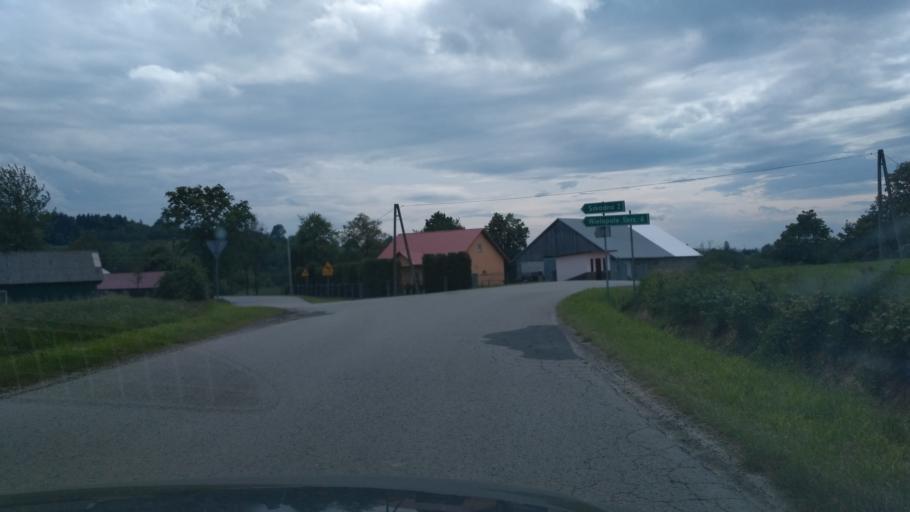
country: PL
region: Subcarpathian Voivodeship
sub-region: Powiat ropczycko-sedziszowski
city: Wielopole Skrzynskie
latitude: 49.9929
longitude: 21.6129
